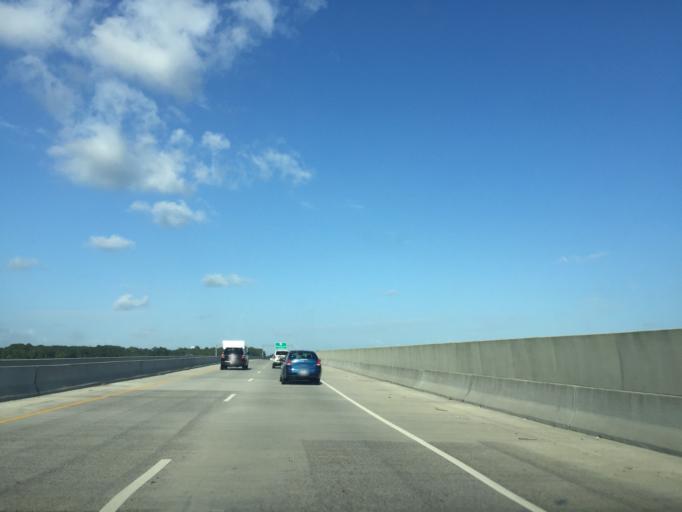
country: US
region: Georgia
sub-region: Chatham County
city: Montgomery
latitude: 31.9755
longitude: -81.1224
